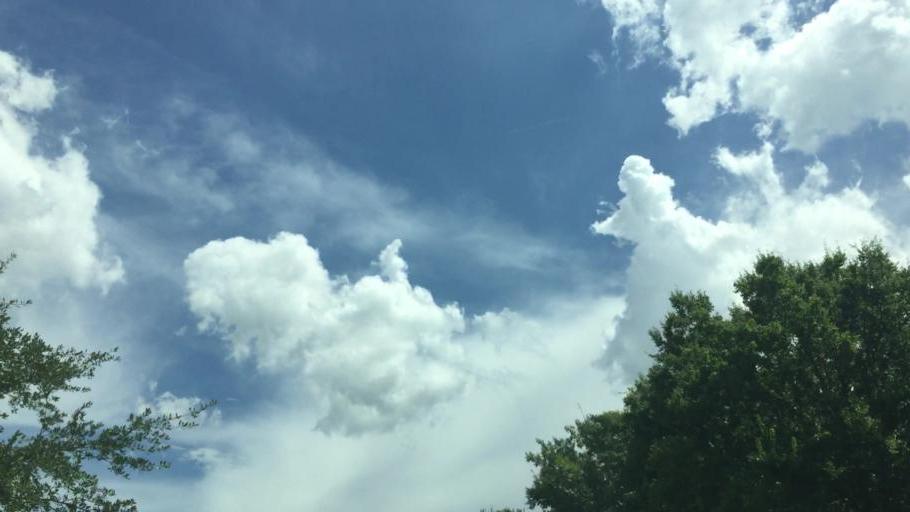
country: US
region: Texas
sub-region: Harris County
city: Bunker Hill Village
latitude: 29.7575
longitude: -95.5886
